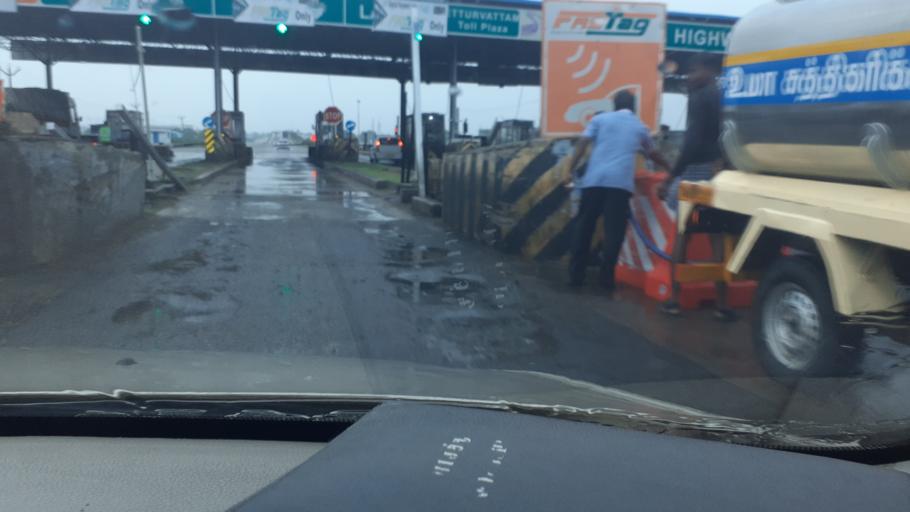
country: IN
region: Tamil Nadu
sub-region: Virudhunagar
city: Sattur
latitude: 9.3857
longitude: 77.9144
